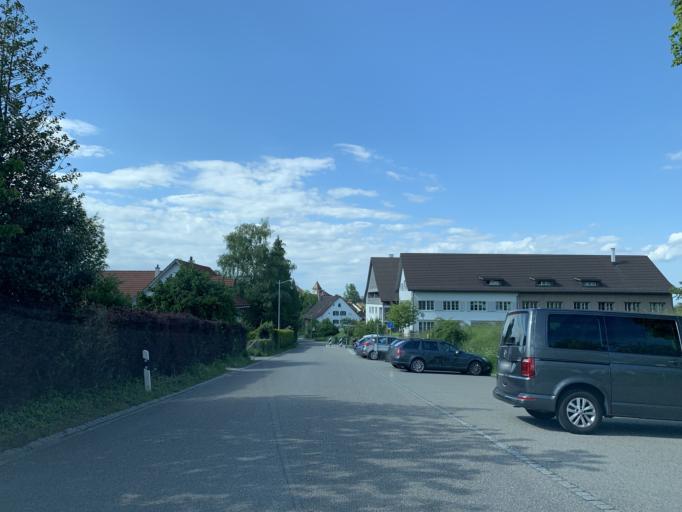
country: CH
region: Zurich
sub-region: Bezirk Winterthur
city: Kollbrunn / Kollbrunn (Dorfkern)
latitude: 47.4529
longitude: 8.7433
